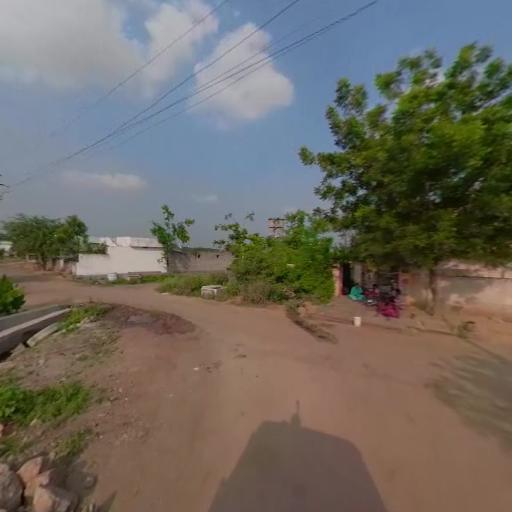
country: IN
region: Telangana
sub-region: Nalgonda
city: Suriapet
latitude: 17.1670
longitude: 79.5071
